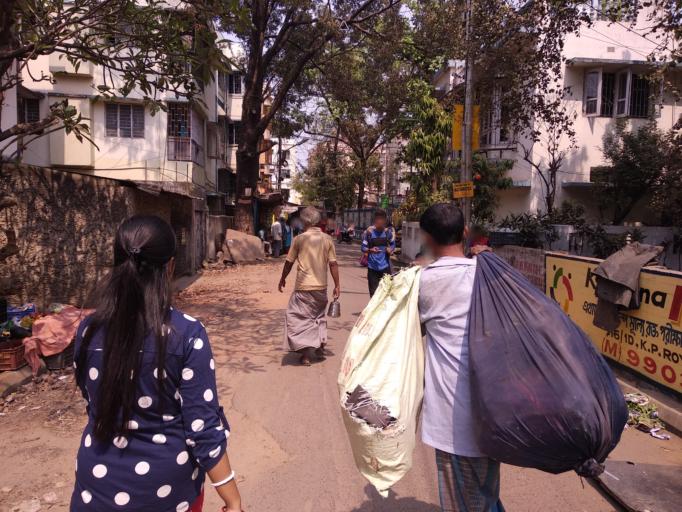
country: IN
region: West Bengal
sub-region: Kolkata
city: Kolkata
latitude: 22.5032
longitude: 88.3786
